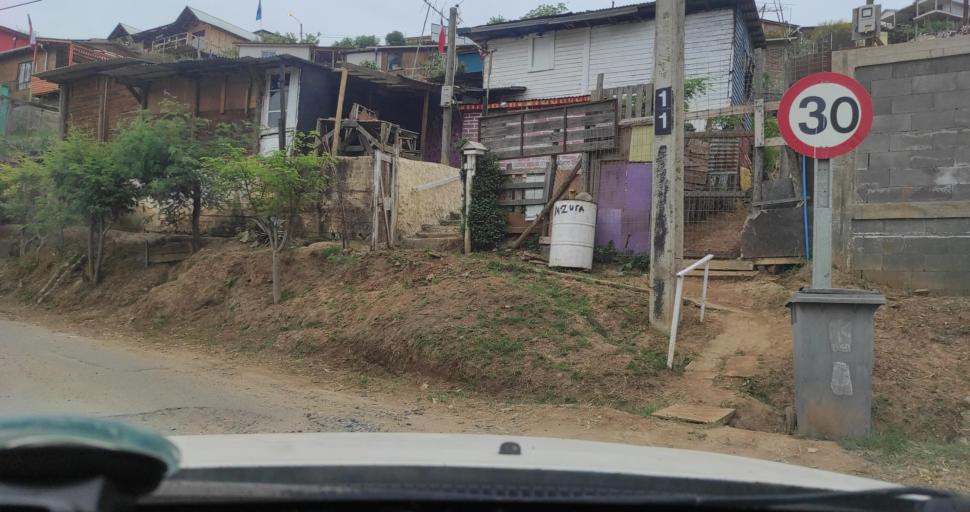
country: CL
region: Valparaiso
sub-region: Provincia de Marga Marga
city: Limache
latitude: -32.9857
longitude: -71.2257
